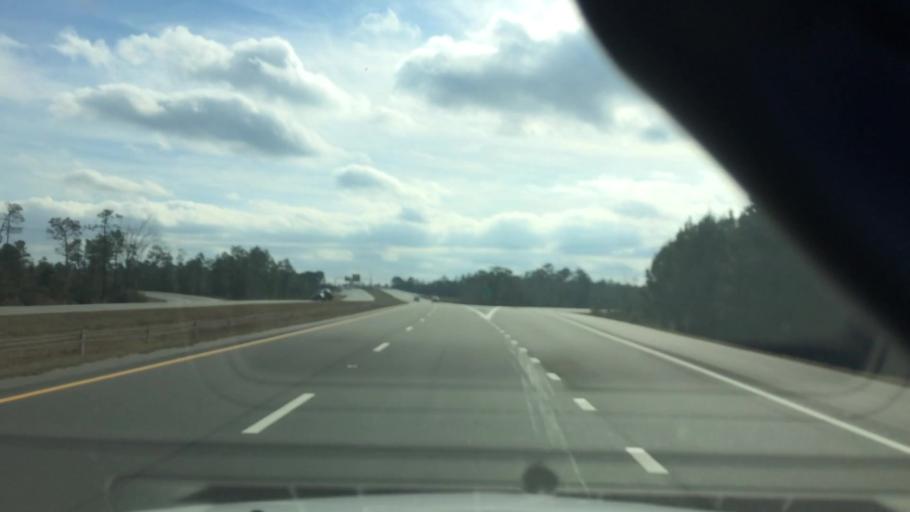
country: US
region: North Carolina
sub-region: Brunswick County
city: Leland
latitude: 34.2642
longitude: -78.0797
